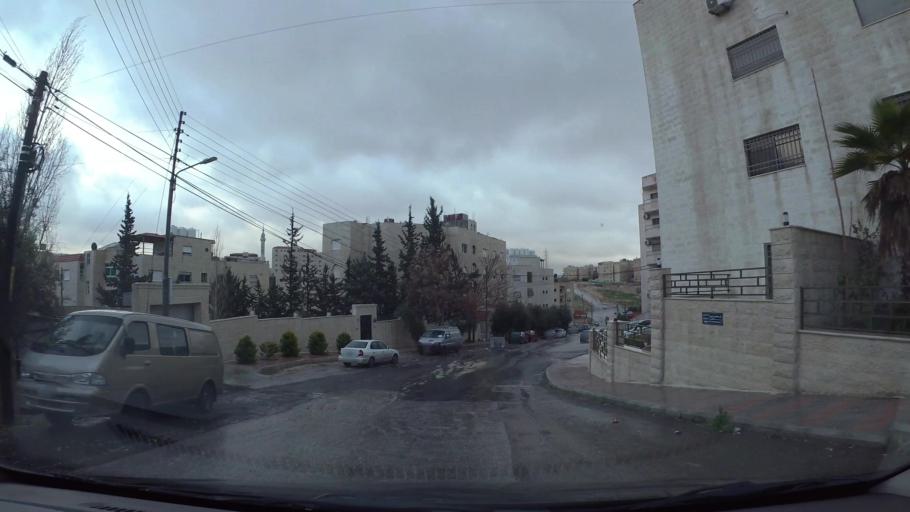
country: JO
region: Amman
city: Amman
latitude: 32.0032
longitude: 35.9298
